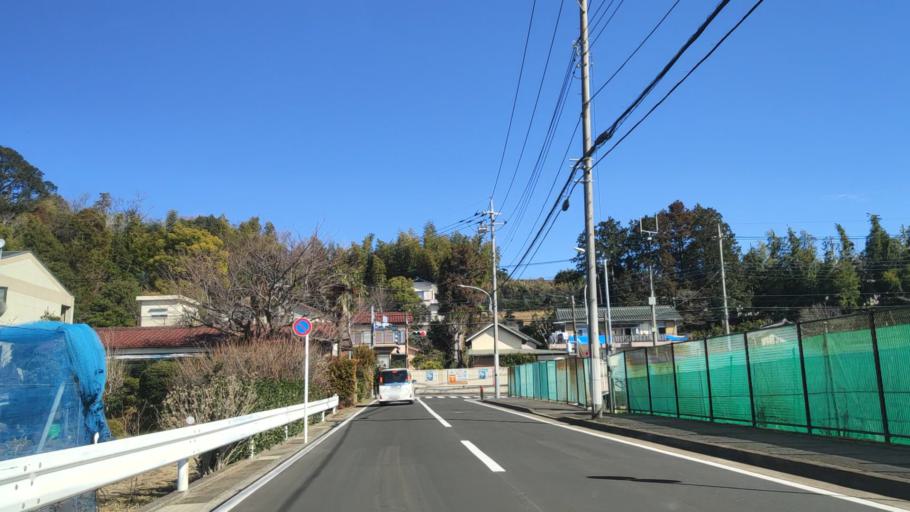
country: JP
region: Tokyo
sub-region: Machida-shi
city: Machida
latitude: 35.5199
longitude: 139.5372
